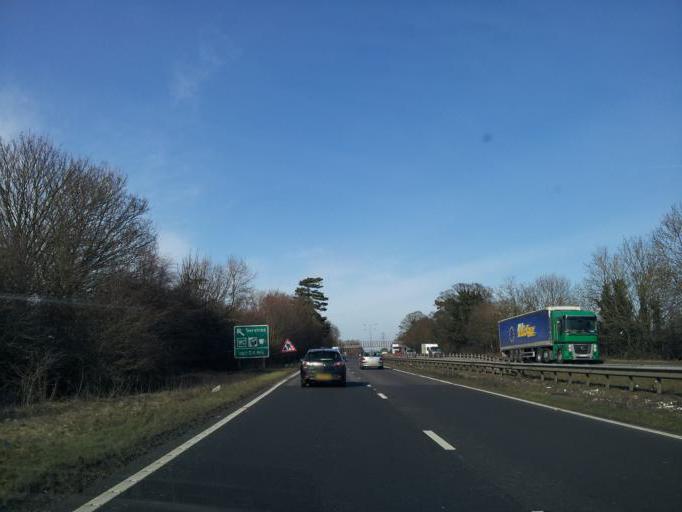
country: GB
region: England
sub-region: Lincolnshire
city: Grantham
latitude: 52.8590
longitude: -0.6292
